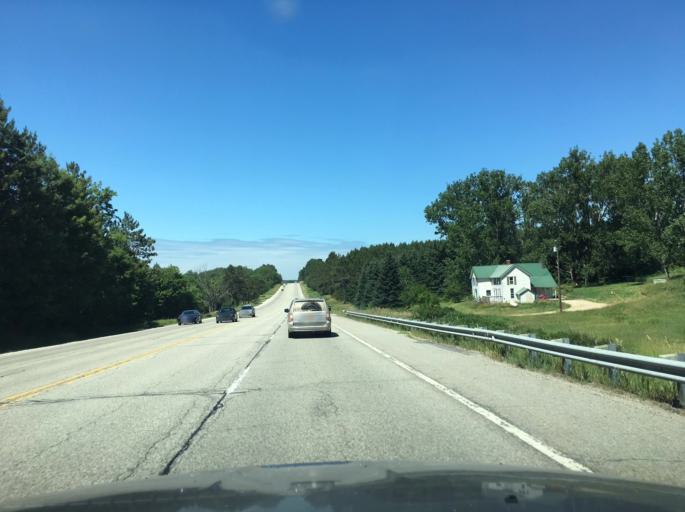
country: US
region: Michigan
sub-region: Osceola County
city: Reed City
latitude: 43.8879
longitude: -85.6055
